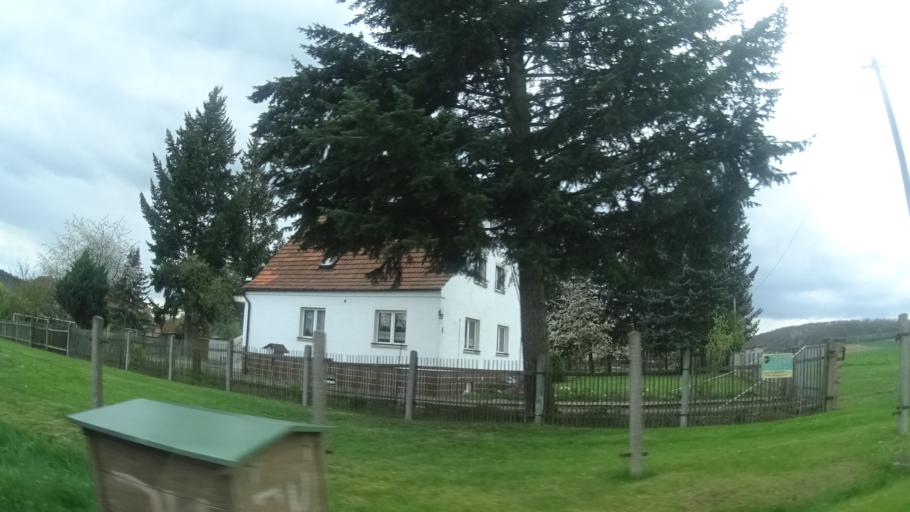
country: DE
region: Thuringia
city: Stadtilm
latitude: 50.7729
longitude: 11.0700
